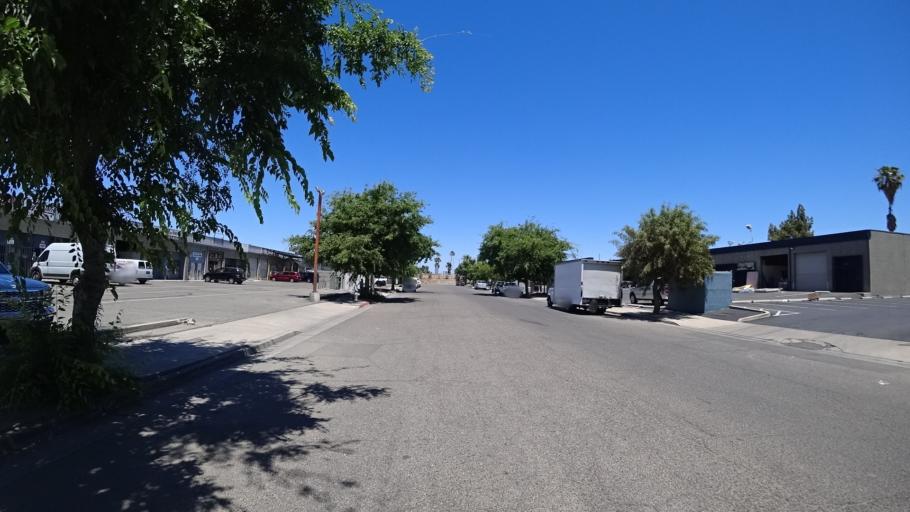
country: US
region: California
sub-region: Fresno County
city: West Park
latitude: 36.7702
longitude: -119.8405
